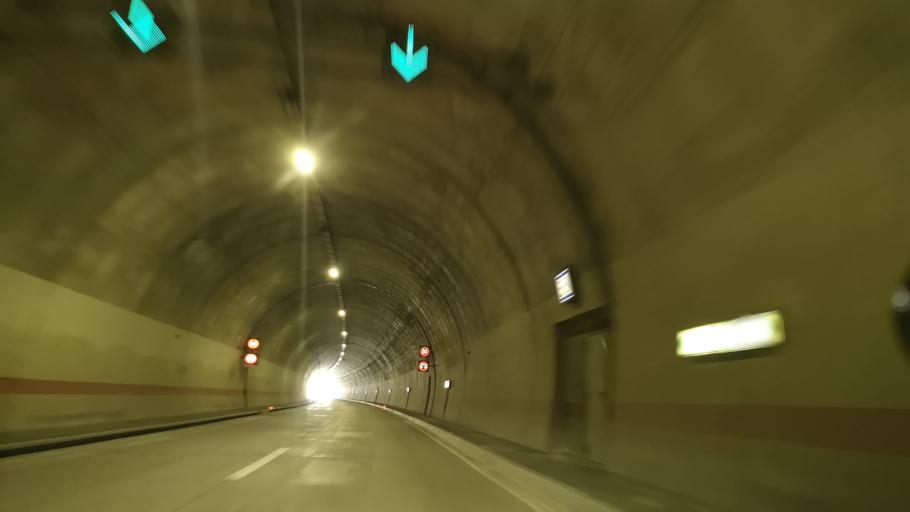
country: RS
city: Prislonica
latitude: 43.9792
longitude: 20.4019
